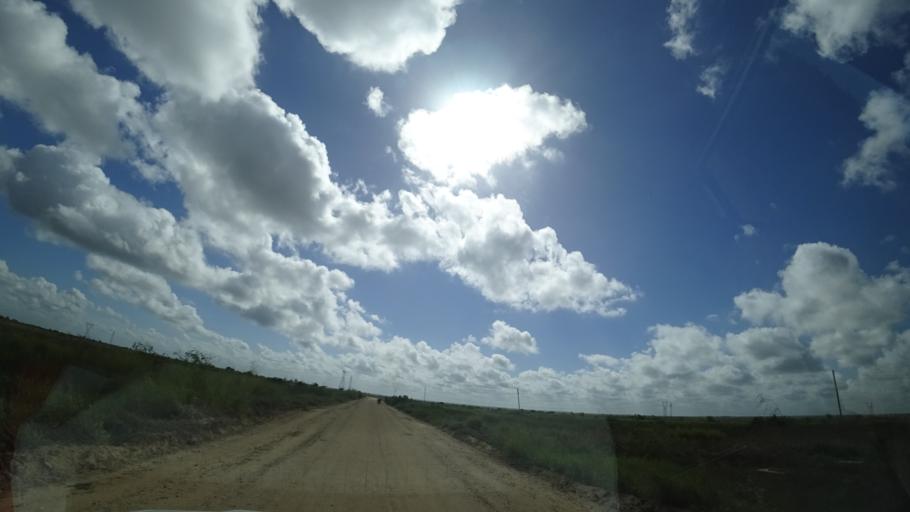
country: MZ
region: Sofala
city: Dondo
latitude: -19.4638
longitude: 34.5614
